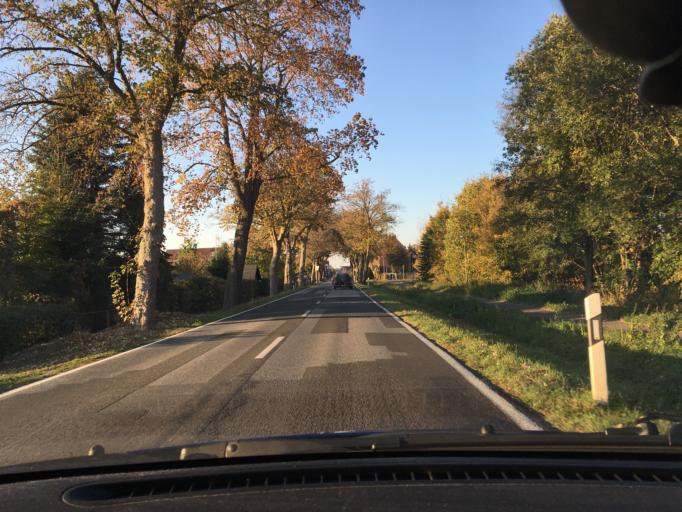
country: DE
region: Mecklenburg-Vorpommern
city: Boizenburg
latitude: 53.3717
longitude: 10.7563
